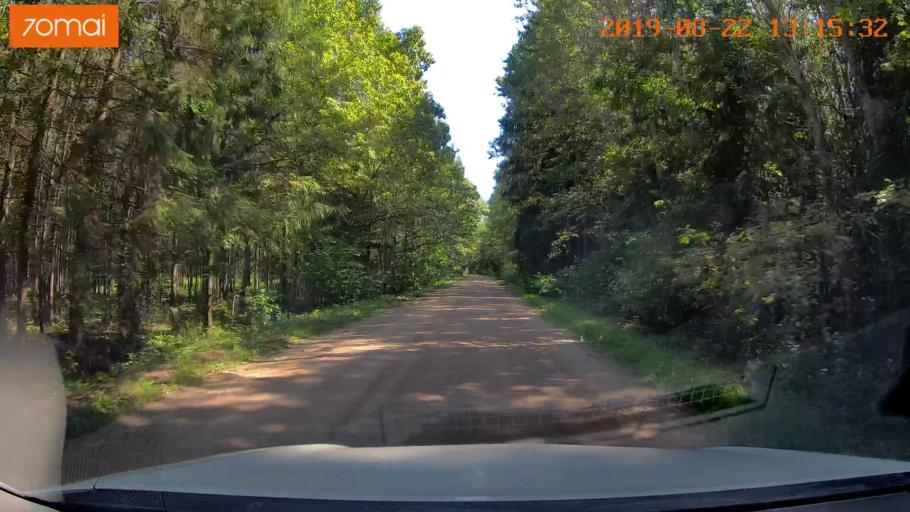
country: BY
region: Minsk
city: Prawdzinski
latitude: 53.2595
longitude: 27.8980
